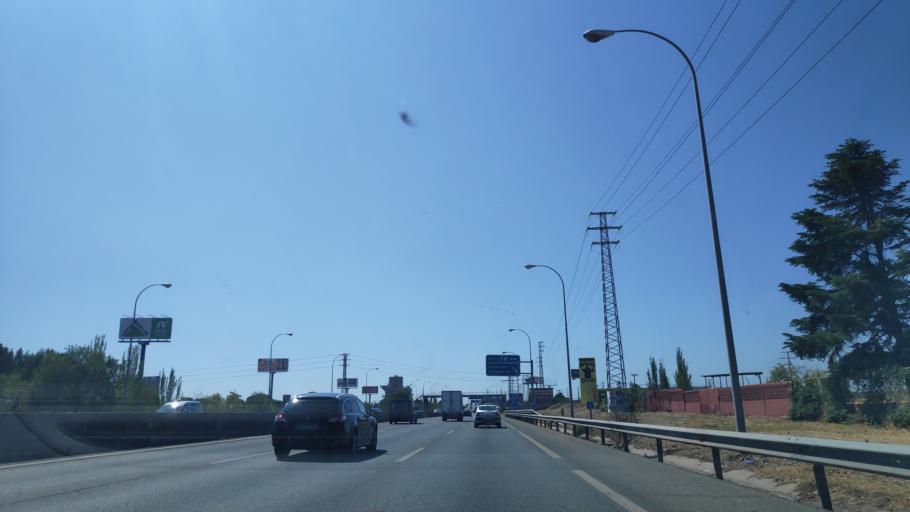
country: ES
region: Madrid
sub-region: Provincia de Madrid
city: Villaverde
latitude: 40.3471
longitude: -3.7233
